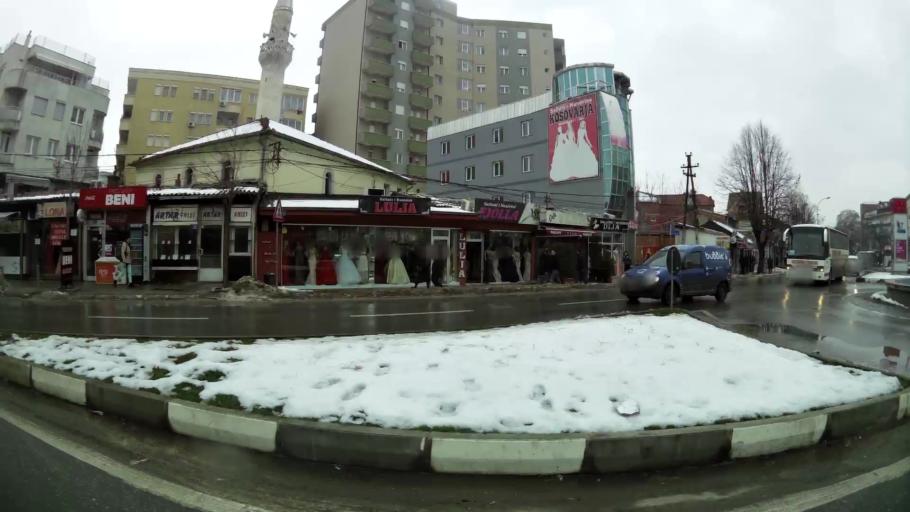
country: XK
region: Pristina
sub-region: Komuna e Prishtines
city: Pristina
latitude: 42.6672
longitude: 21.1641
